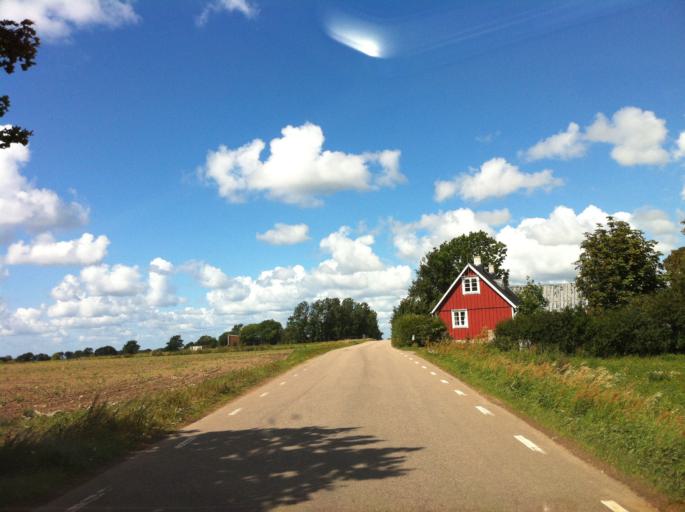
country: SE
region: Skane
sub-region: Angelholms Kommun
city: Strovelstorp
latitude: 56.1835
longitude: 12.8459
